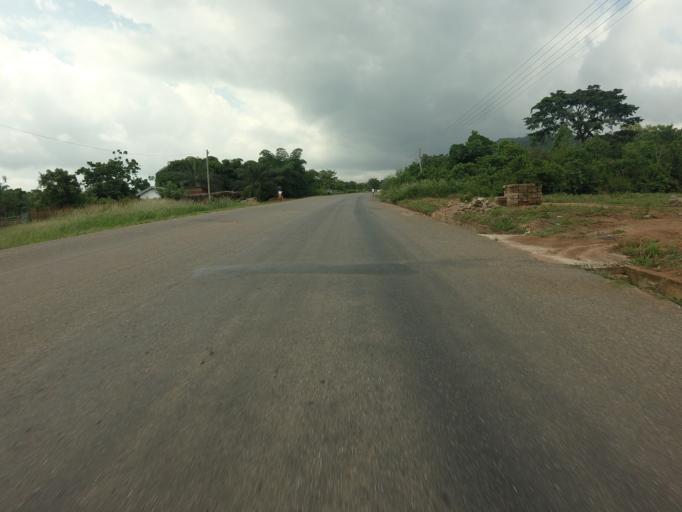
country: GH
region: Volta
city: Kpandu
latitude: 6.9031
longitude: 0.4375
